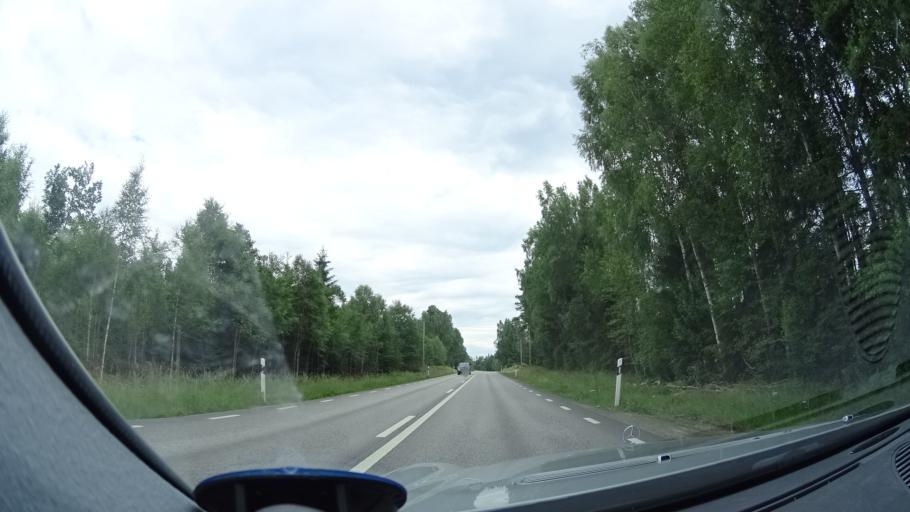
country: SE
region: Kronoberg
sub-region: Tingsryds Kommun
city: Tingsryd
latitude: 56.5017
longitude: 14.9953
